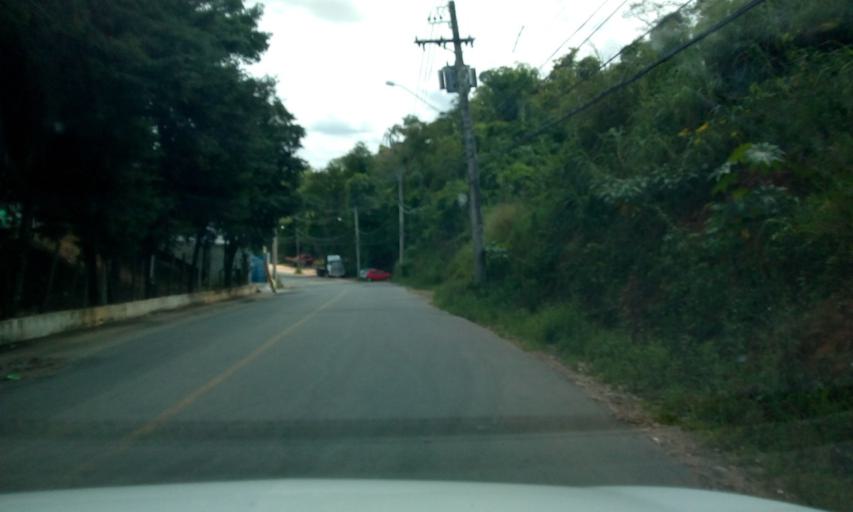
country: BR
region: Sao Paulo
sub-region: Itupeva
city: Itupeva
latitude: -23.1478
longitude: -47.0547
